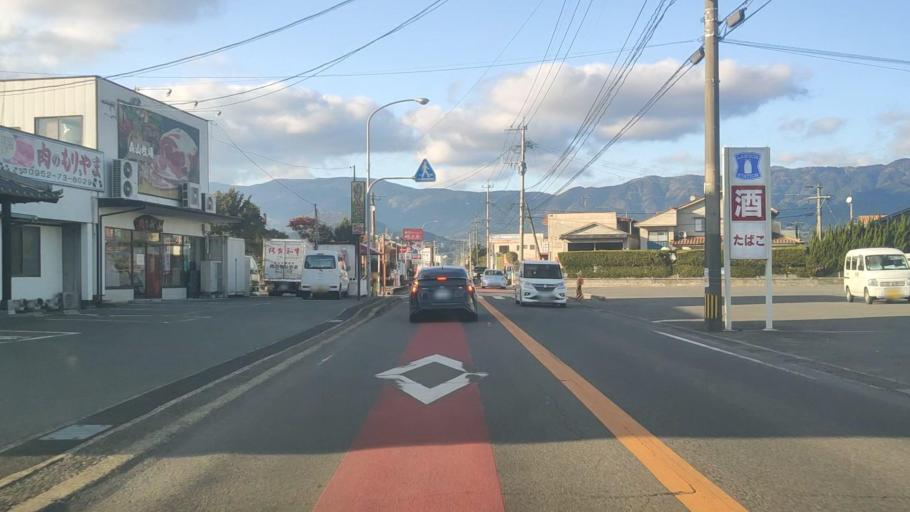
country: JP
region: Saga Prefecture
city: Saga-shi
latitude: 33.2812
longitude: 130.2120
